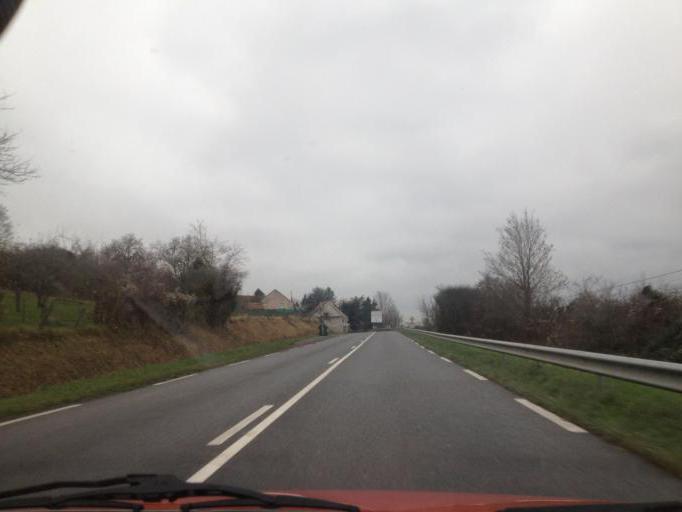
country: FR
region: Auvergne
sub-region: Departement de l'Allier
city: Saint-Germain-des-Fosses
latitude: 46.2407
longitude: 3.4276
